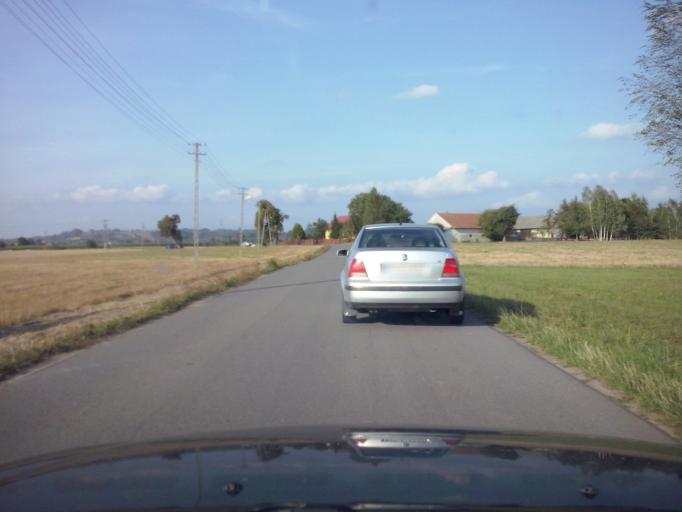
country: PL
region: Subcarpathian Voivodeship
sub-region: Powiat nizanski
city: Krzeszow
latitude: 50.3812
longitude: 22.3247
